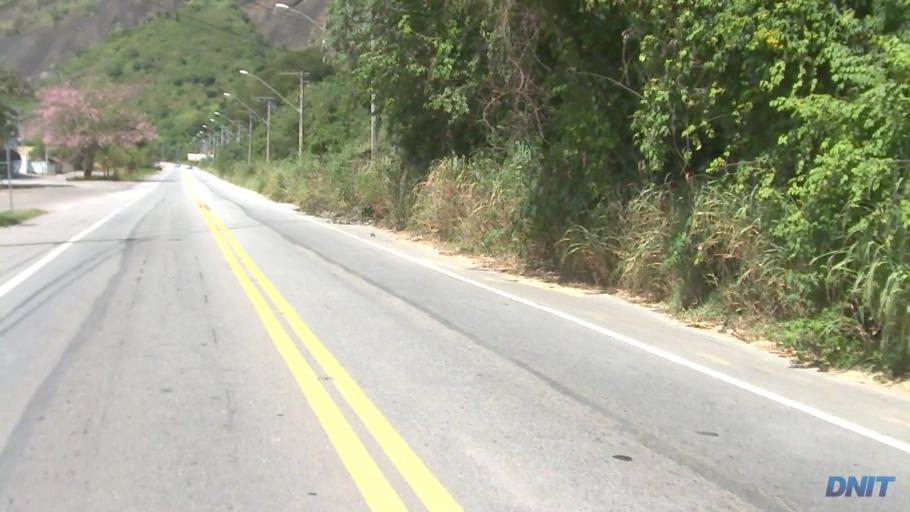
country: BR
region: Minas Gerais
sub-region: Timoteo
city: Timoteo
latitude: -19.5423
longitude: -42.6851
